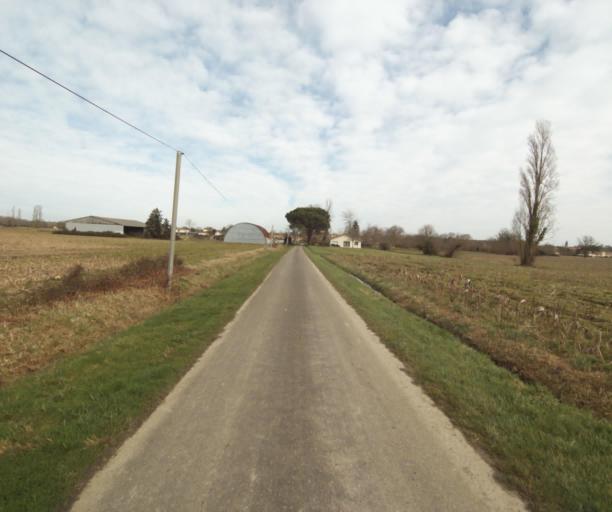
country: FR
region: Aquitaine
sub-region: Departement des Landes
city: Gabarret
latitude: 43.9809
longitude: 0.0019
